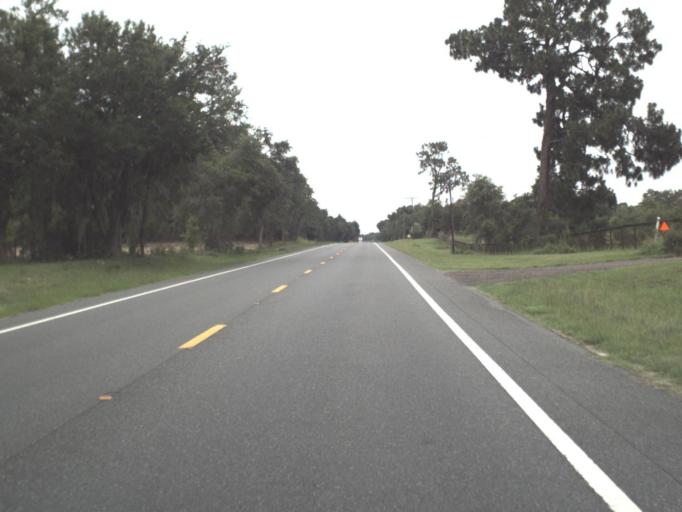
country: US
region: Florida
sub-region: Levy County
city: Williston Highlands
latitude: 29.2370
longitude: -82.4412
